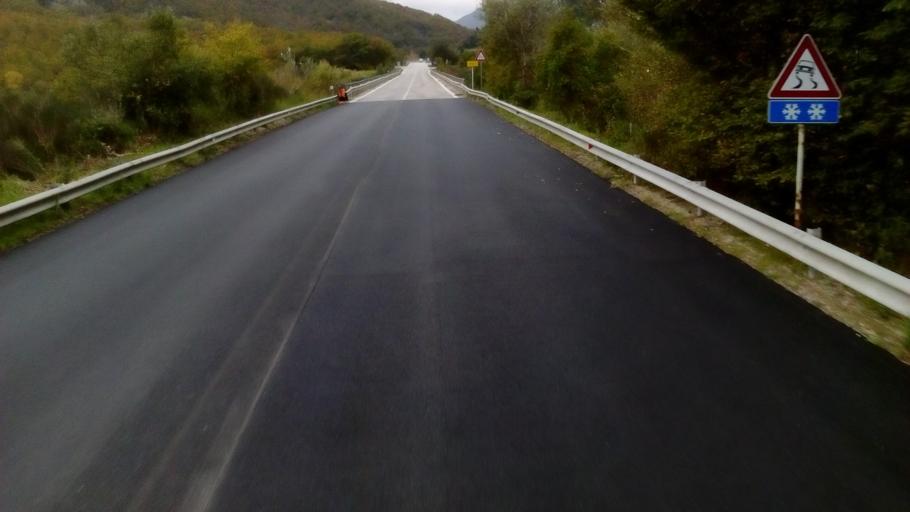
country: IT
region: Molise
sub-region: Provincia di Campobasso
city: Montemitro
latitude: 41.9052
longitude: 14.6469
